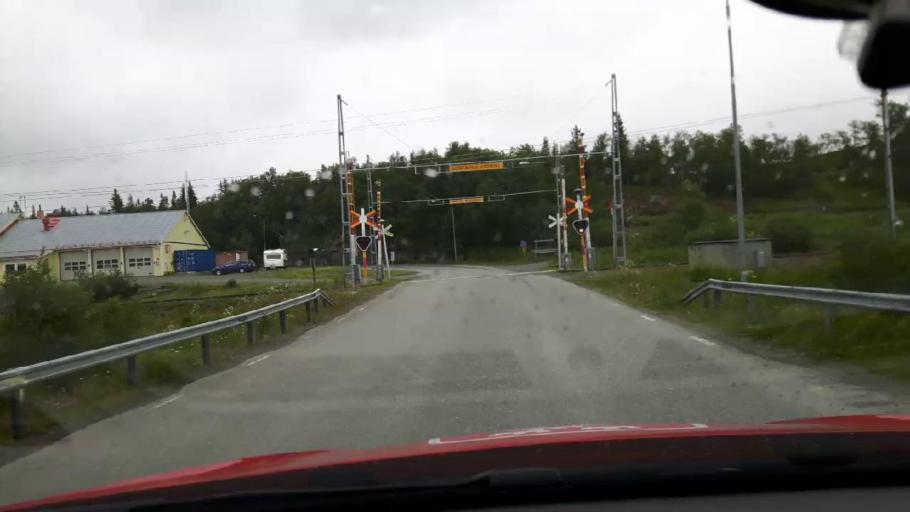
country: NO
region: Nord-Trondelag
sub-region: Meraker
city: Meraker
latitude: 63.3134
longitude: 12.1125
